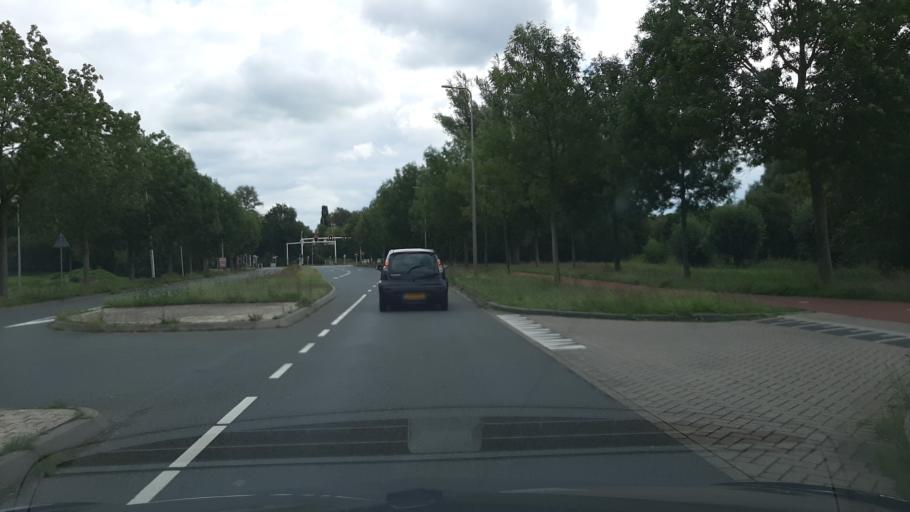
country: NL
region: Overijssel
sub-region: Gemeente Zwolle
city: Zwolle
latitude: 52.5324
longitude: 6.0885
